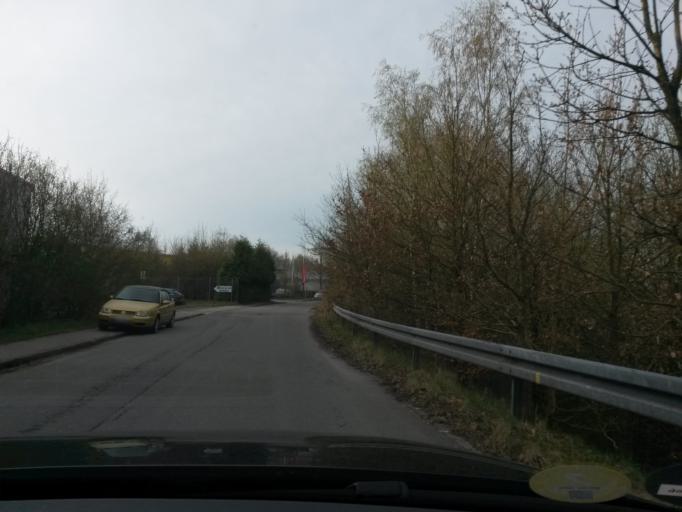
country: DE
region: North Rhine-Westphalia
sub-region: Regierungsbezirk Arnsberg
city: Luedenscheid
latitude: 51.2461
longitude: 7.5960
